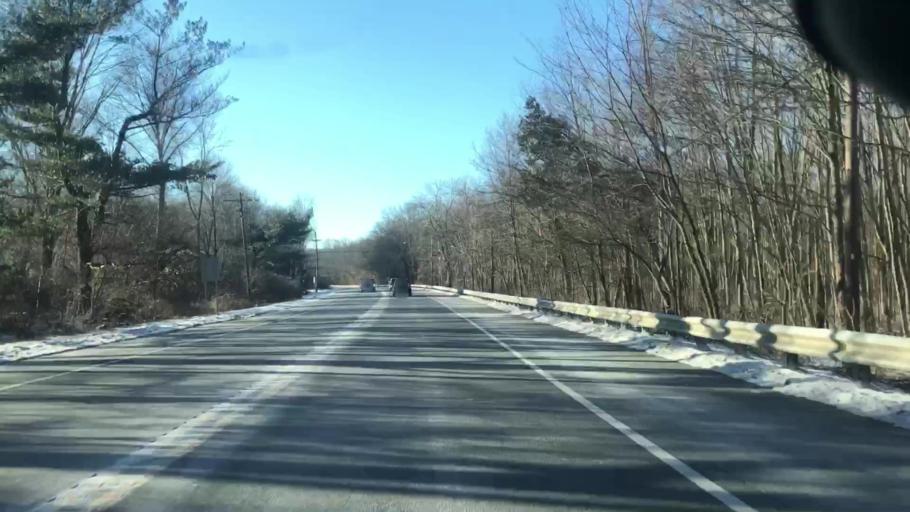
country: US
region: New Jersey
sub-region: Morris County
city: Chester
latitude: 40.8194
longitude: -74.7105
